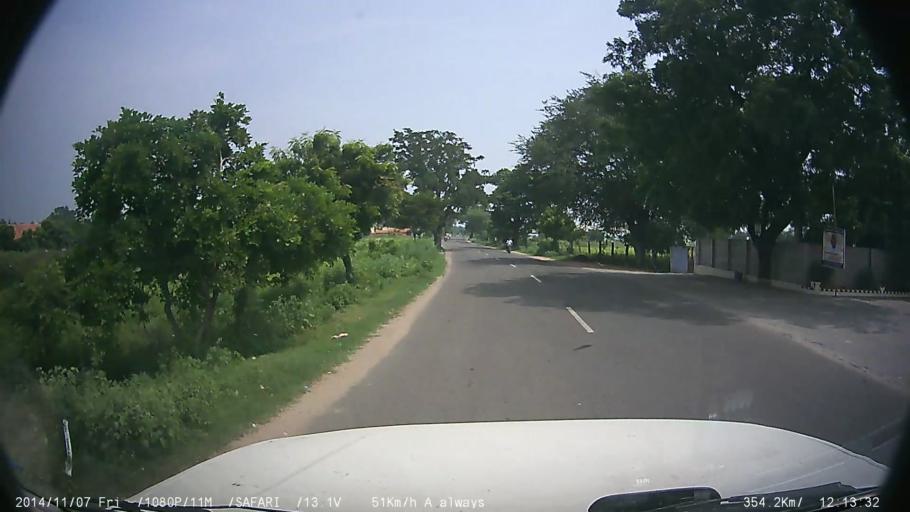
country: IN
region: Tamil Nadu
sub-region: Tiruppur
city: Tiruppur
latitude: 11.1017
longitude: 77.2768
